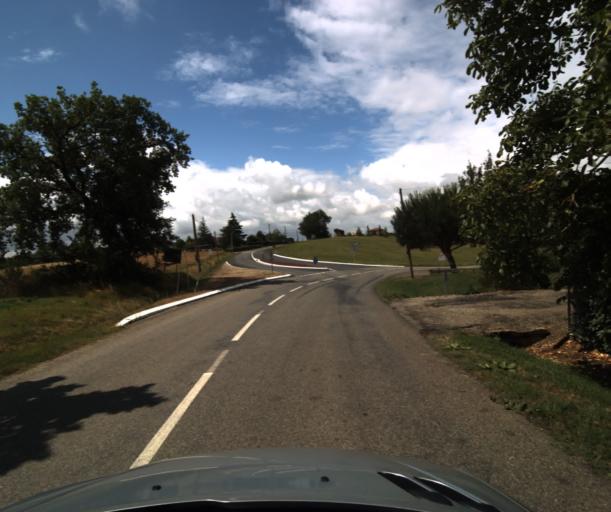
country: FR
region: Midi-Pyrenees
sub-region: Departement du Tarn-et-Garonne
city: Lavit
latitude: 43.9534
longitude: 0.9132
